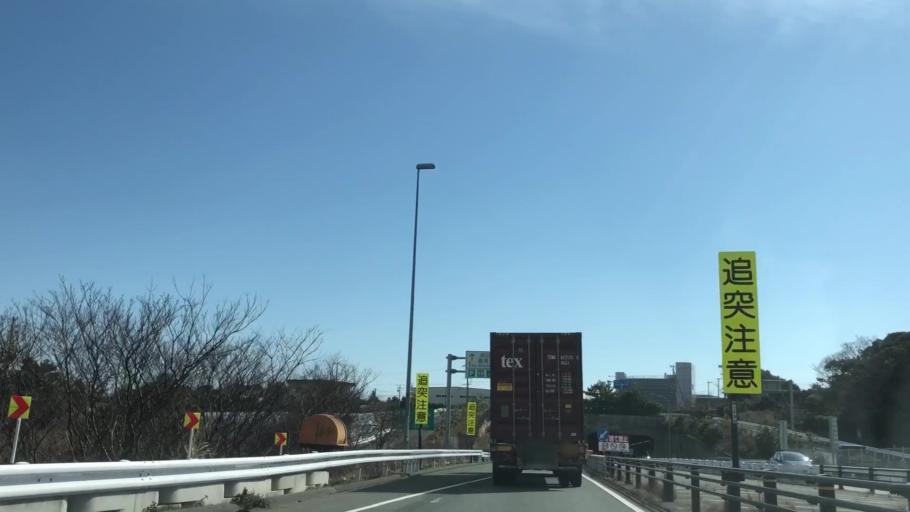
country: JP
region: Shizuoka
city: Kosai-shi
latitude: 34.6875
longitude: 137.4901
